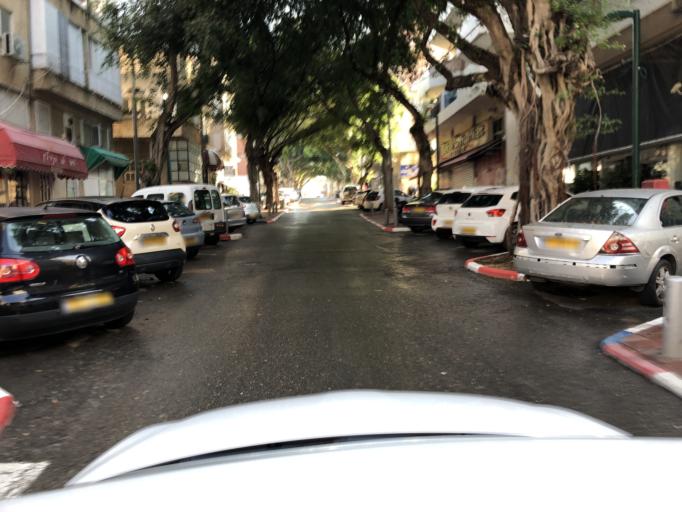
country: IL
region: Tel Aviv
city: Ramat Gan
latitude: 32.0912
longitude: 34.8185
